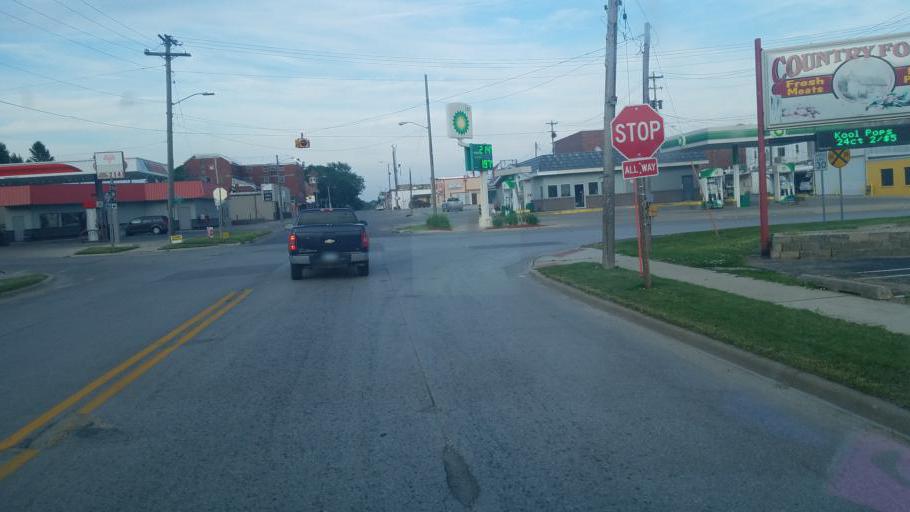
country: US
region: Iowa
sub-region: Benton County
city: Belle Plaine
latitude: 41.8970
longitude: -92.2786
